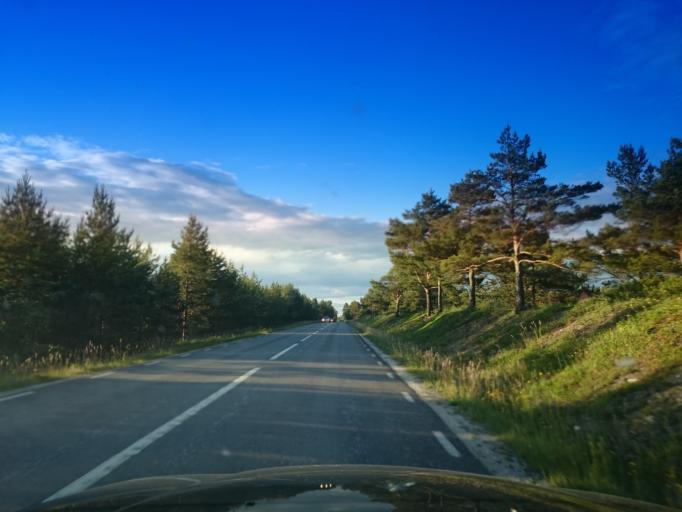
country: SE
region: Gotland
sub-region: Gotland
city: Hemse
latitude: 57.3405
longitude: 18.3786
